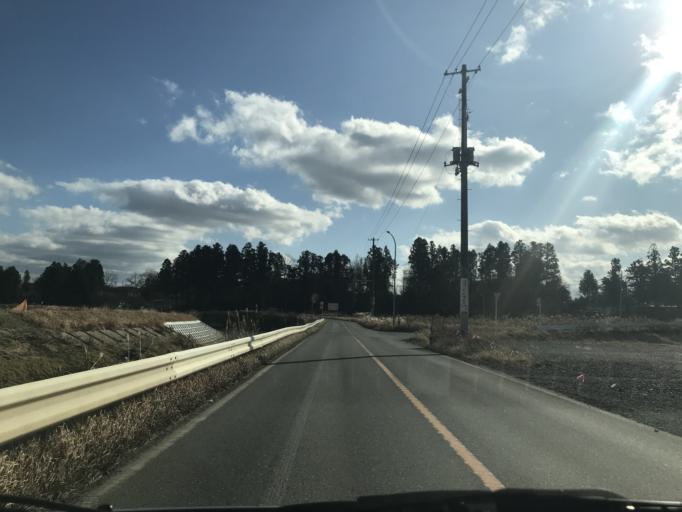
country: JP
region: Miyagi
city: Kogota
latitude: 38.7224
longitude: 141.0650
